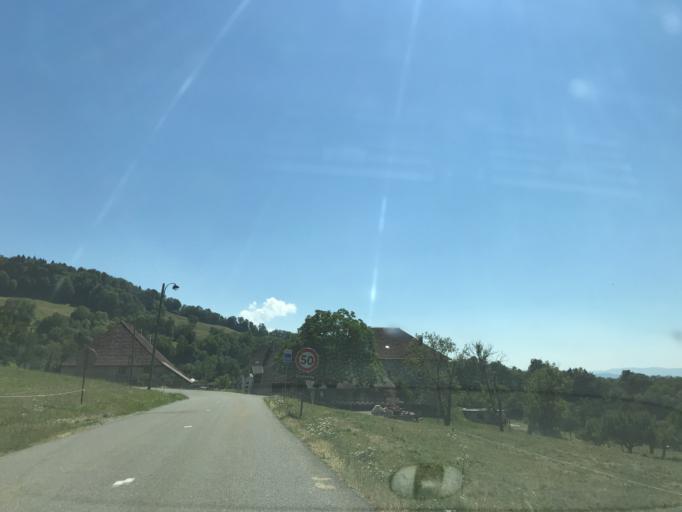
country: FR
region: Rhone-Alpes
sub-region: Departement de la Haute-Savoie
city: Villaz
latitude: 45.9639
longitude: 6.2154
